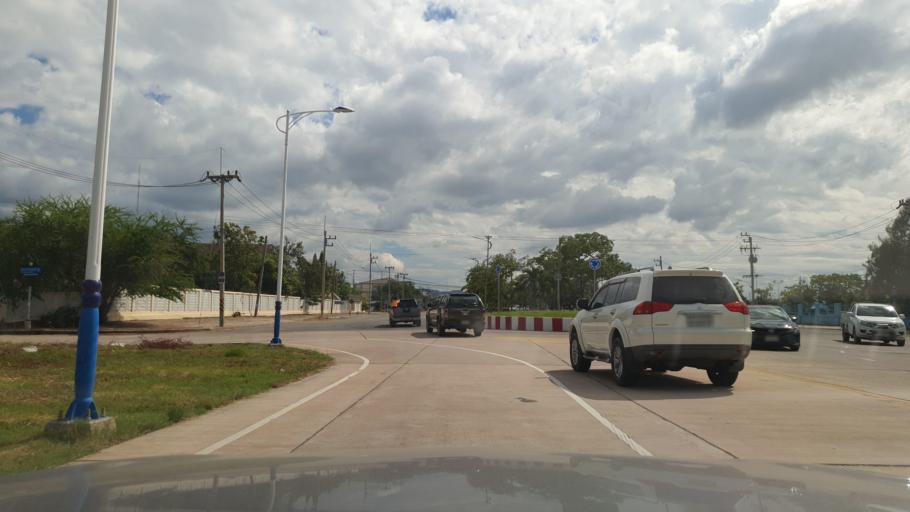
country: TH
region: Chon Buri
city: Chon Buri
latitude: 13.3446
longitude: 100.9497
